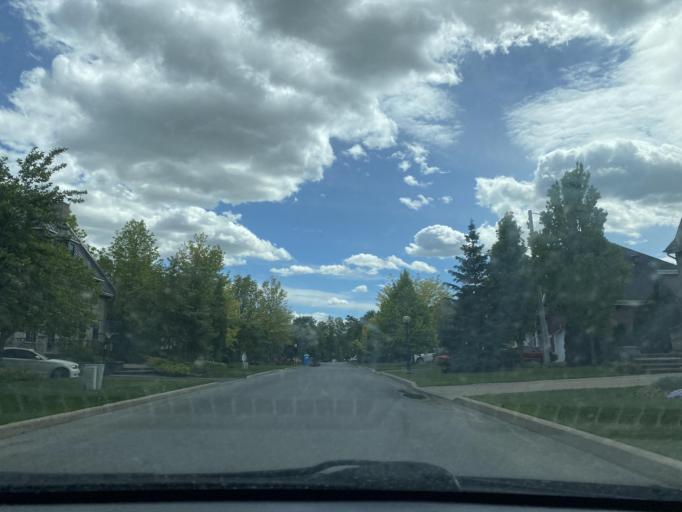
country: CA
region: Quebec
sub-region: Monteregie
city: Chambly
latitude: 45.4712
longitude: -73.2898
